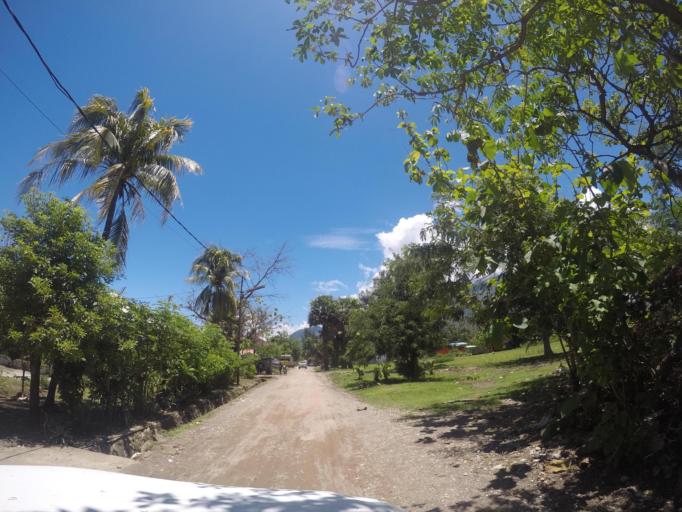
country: TL
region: Bobonaro
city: Maliana
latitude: -8.9918
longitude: 125.2215
